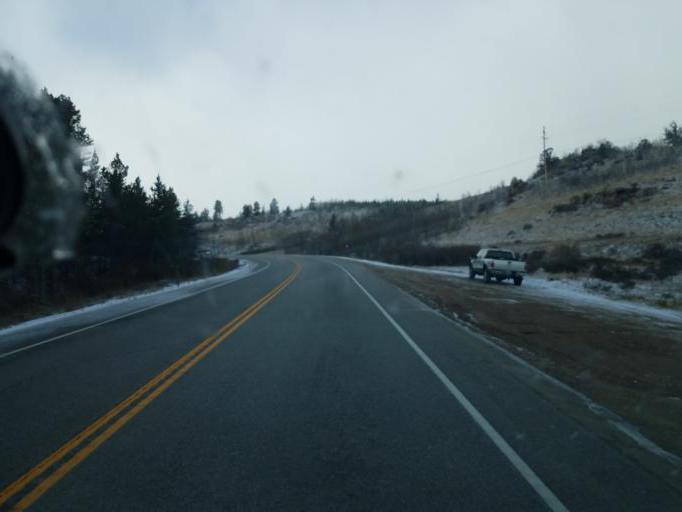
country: US
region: Colorado
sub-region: Clear Creek County
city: Georgetown
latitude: 39.4422
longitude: -105.7464
